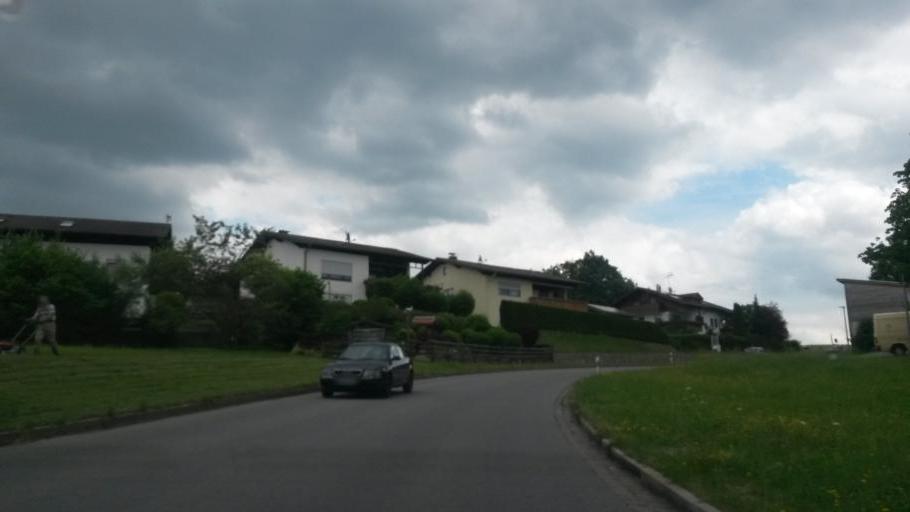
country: DE
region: Bavaria
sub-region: Upper Bavaria
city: Bad Endorf
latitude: 47.9111
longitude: 12.3047
